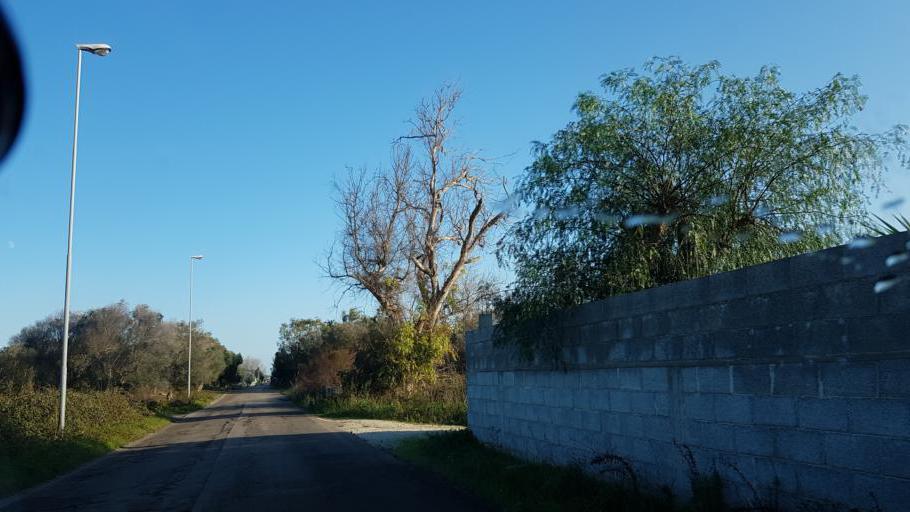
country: IT
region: Apulia
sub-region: Provincia di Brindisi
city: Torchiarolo
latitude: 40.5040
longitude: 18.1058
